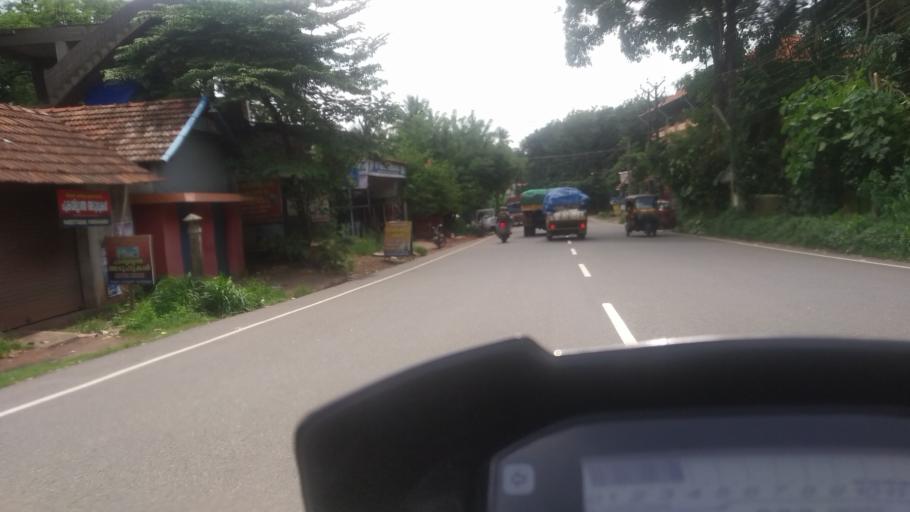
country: IN
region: Kerala
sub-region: Ernakulam
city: Aluva
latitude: 10.1261
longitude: 76.3313
